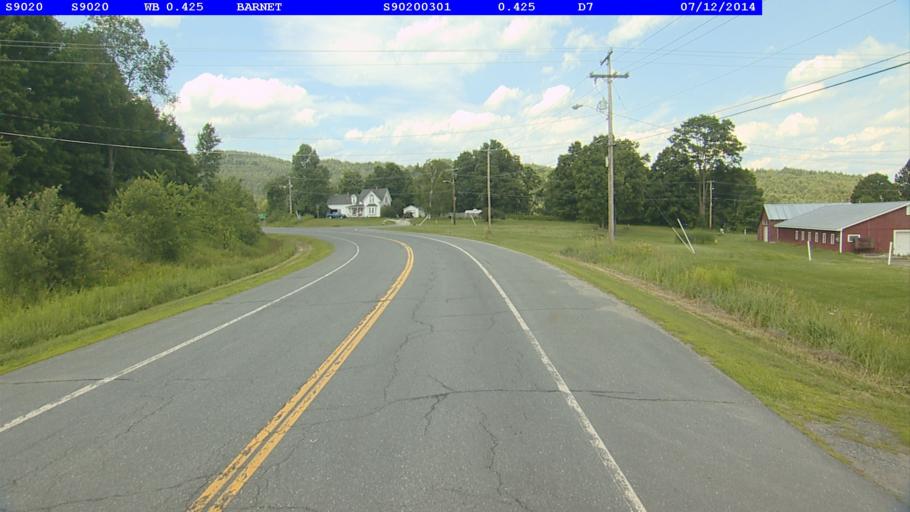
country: US
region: Vermont
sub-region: Caledonia County
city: Saint Johnsbury
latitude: 44.2959
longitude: -72.0557
